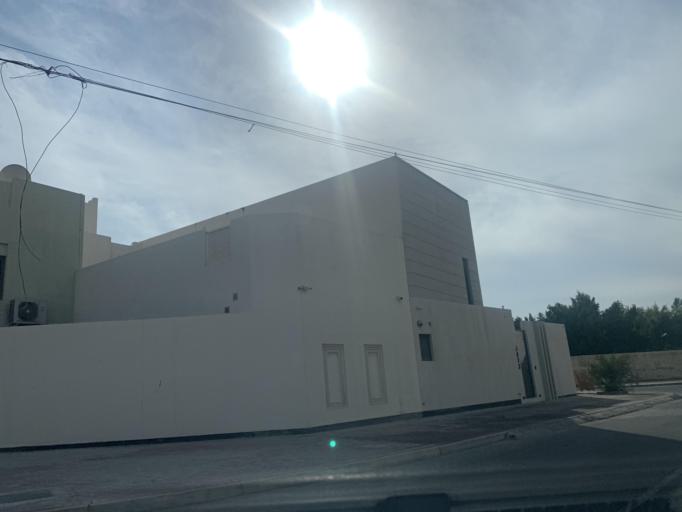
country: BH
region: Central Governorate
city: Madinat Hamad
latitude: 26.1233
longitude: 50.4753
